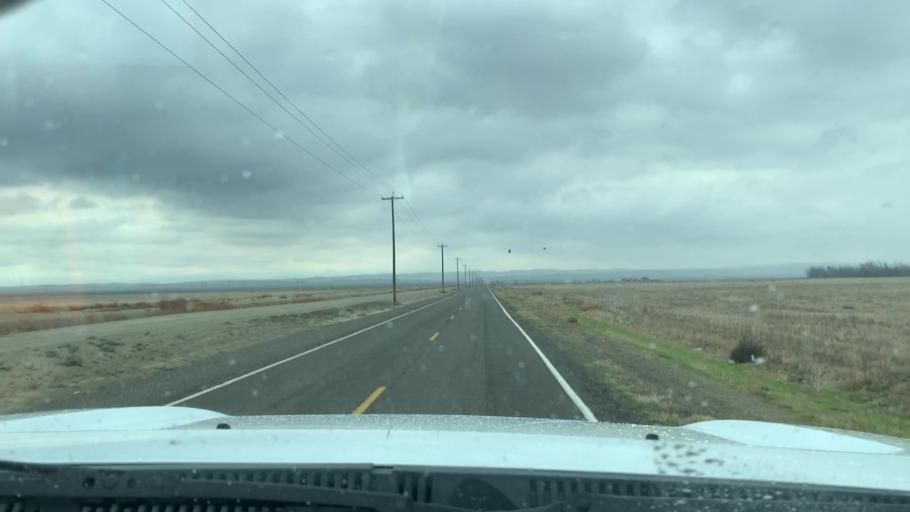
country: US
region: California
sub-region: Kings County
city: Kettleman City
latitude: 35.9341
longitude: -119.8551
